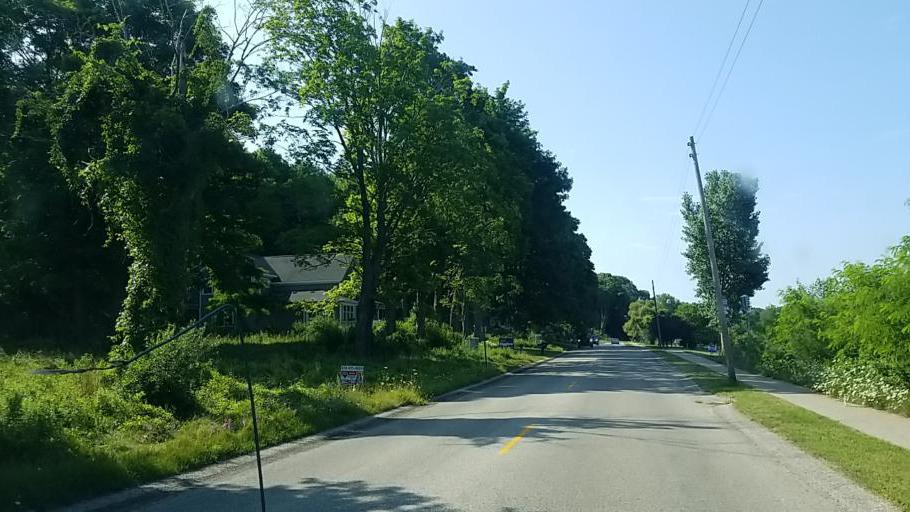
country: US
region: Michigan
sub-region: Muskegon County
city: Whitehall
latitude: 43.3943
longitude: -86.3535
